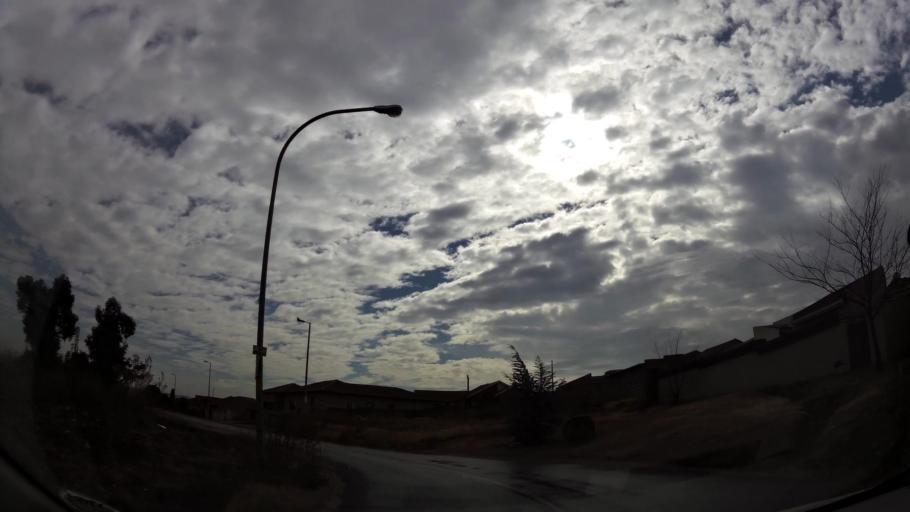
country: ZA
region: Gauteng
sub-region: Ekurhuleni Metropolitan Municipality
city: Germiston
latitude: -26.3138
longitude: 28.1779
